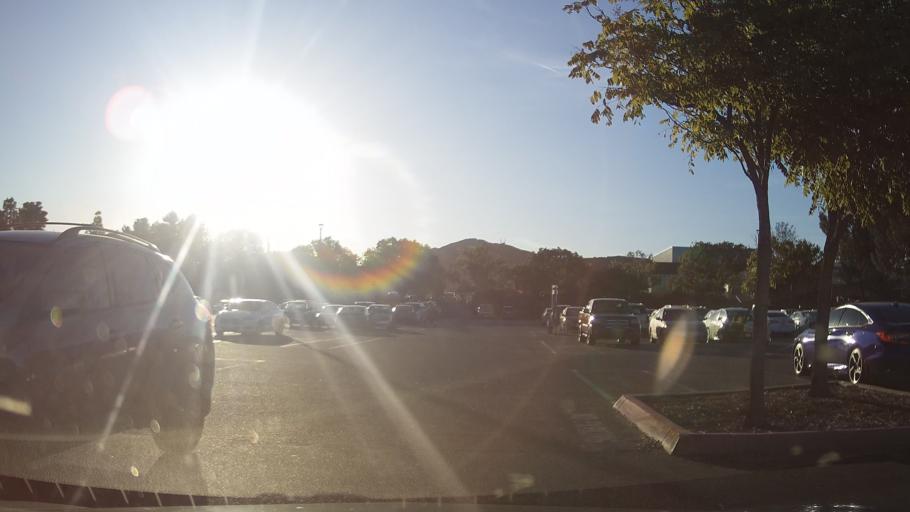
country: US
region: California
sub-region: San Diego County
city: Santee
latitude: 32.8142
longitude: -117.0049
